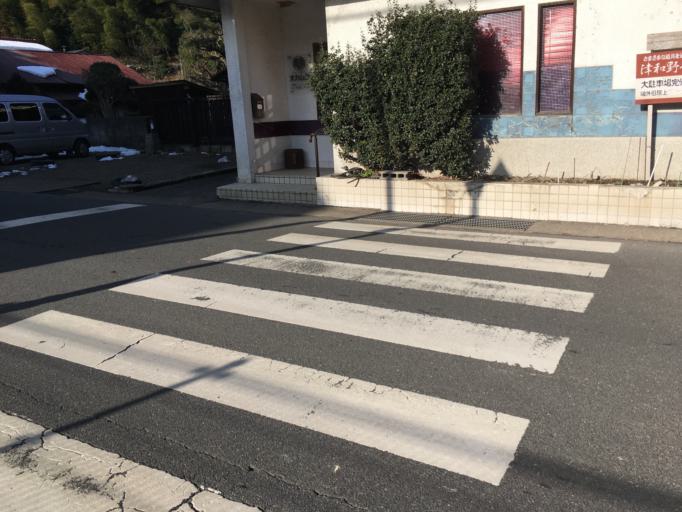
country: JP
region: Shimane
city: Masuda
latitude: 34.4695
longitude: 131.7731
